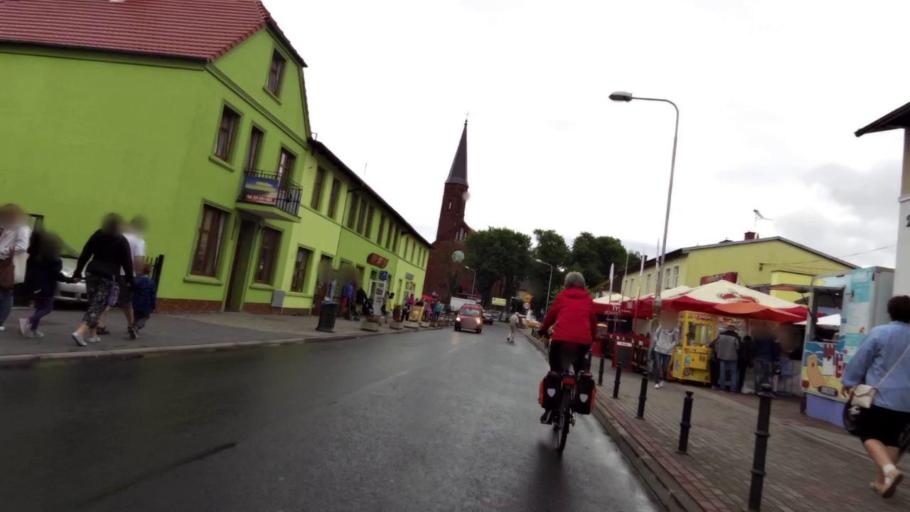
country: PL
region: West Pomeranian Voivodeship
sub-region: Powiat koszalinski
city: Mielno
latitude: 54.2490
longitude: 15.9571
